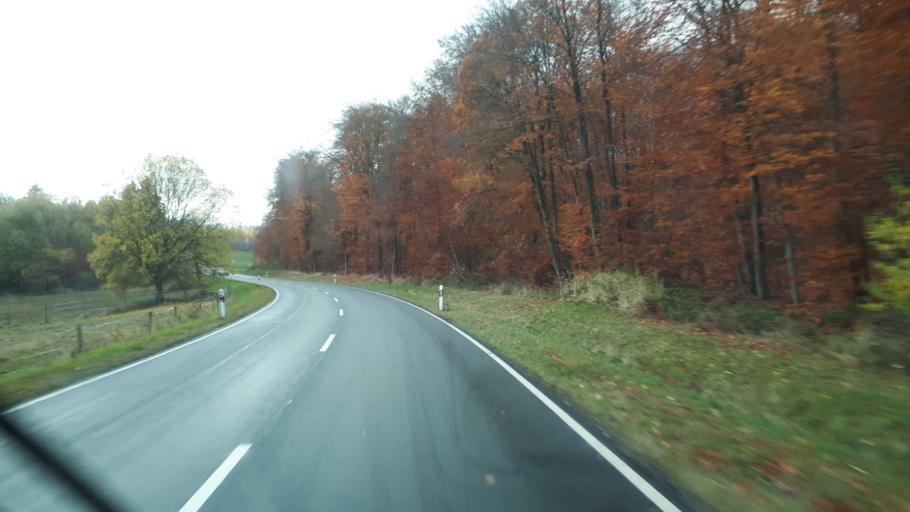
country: DE
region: Rheinland-Pfalz
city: Kaisersesch
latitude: 50.2235
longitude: 7.1271
